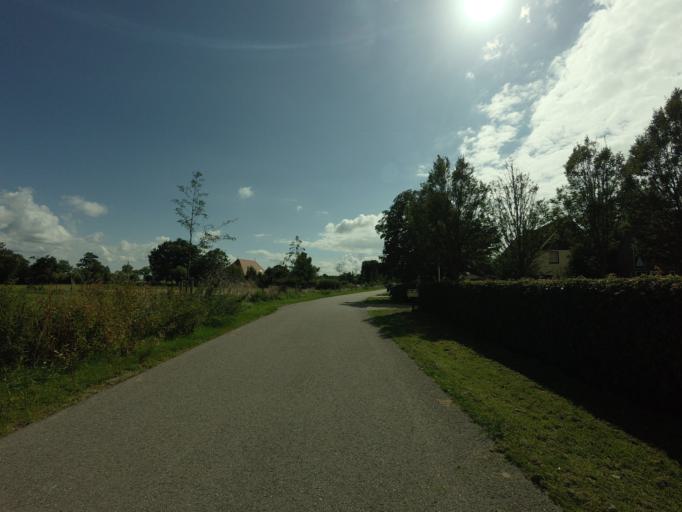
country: NL
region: Friesland
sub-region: Sudwest Fryslan
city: IJlst
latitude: 52.9993
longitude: 5.6478
